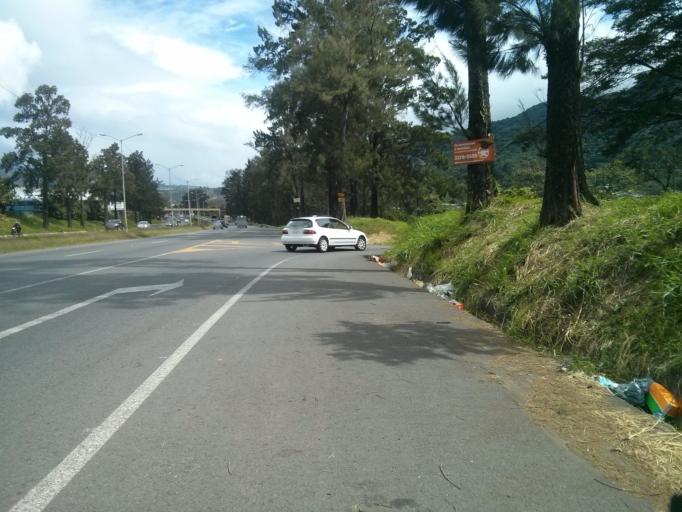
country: CR
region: Cartago
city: San Diego
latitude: 9.9002
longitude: -84.0015
